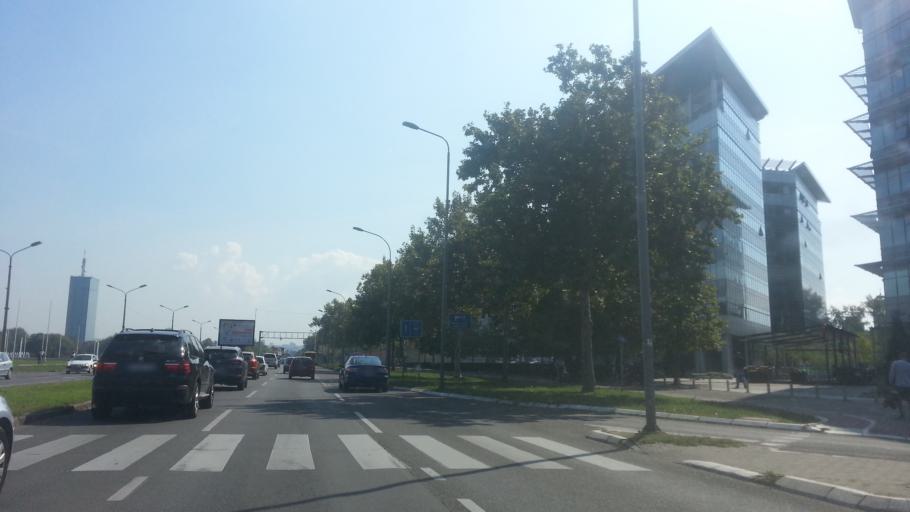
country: RS
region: Central Serbia
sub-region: Belgrade
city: Novi Beograd
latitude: 44.8194
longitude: 20.4237
